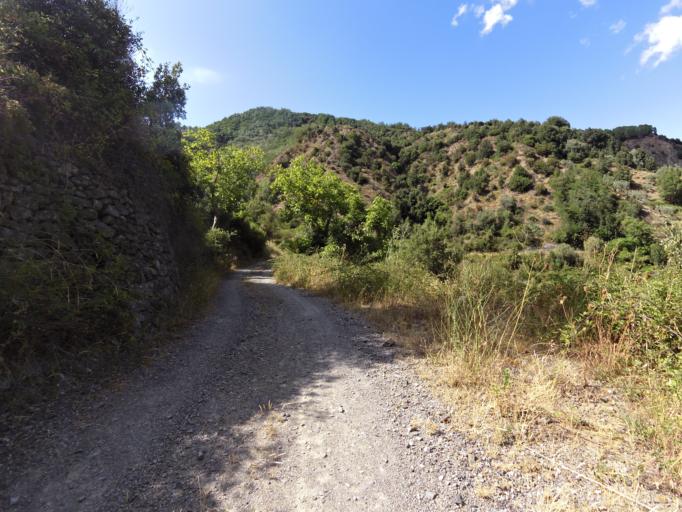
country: IT
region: Calabria
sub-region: Provincia di Reggio Calabria
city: Pazzano
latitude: 38.4721
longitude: 16.4230
